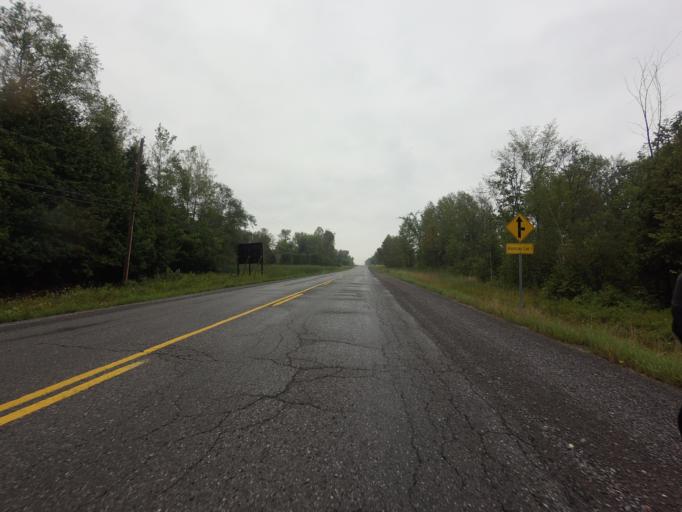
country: CA
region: Ontario
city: Carleton Place
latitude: 45.1510
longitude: -76.3092
